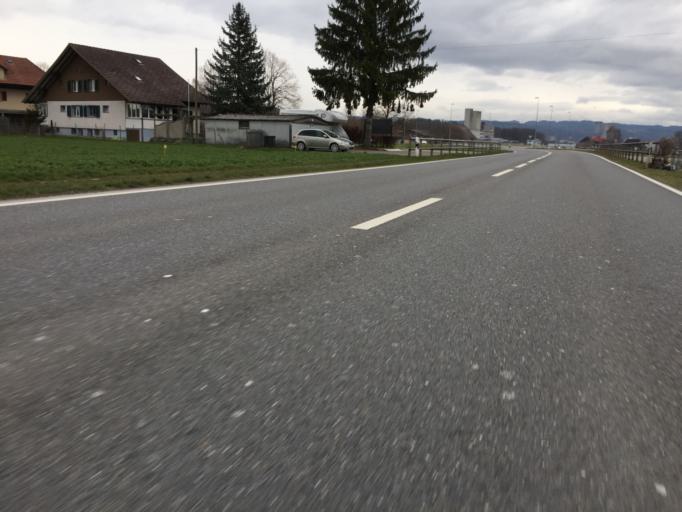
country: CH
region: Bern
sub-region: Emmental District
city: Kirchberg
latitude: 47.0761
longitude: 7.5807
